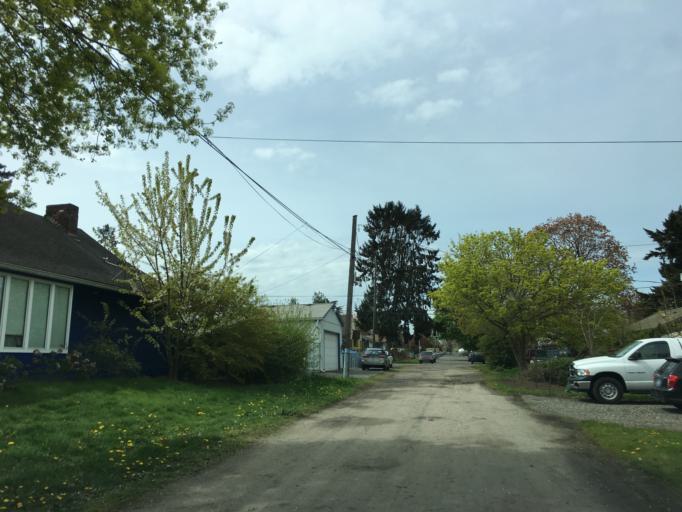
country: US
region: Oregon
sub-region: Multnomah County
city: Lents
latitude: 45.5579
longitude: -122.5681
